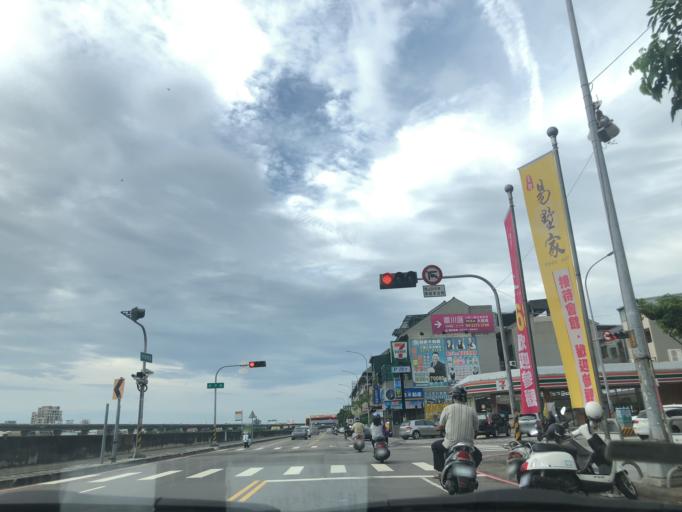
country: TW
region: Taiwan
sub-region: Taichung City
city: Taichung
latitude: 24.1021
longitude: 120.6950
